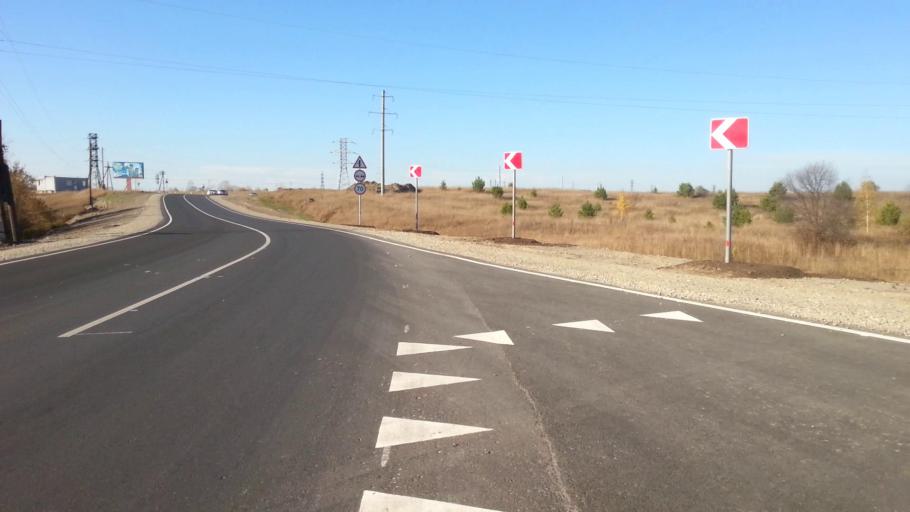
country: RU
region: Altai Krai
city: Sannikovo
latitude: 53.3282
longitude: 83.9410
